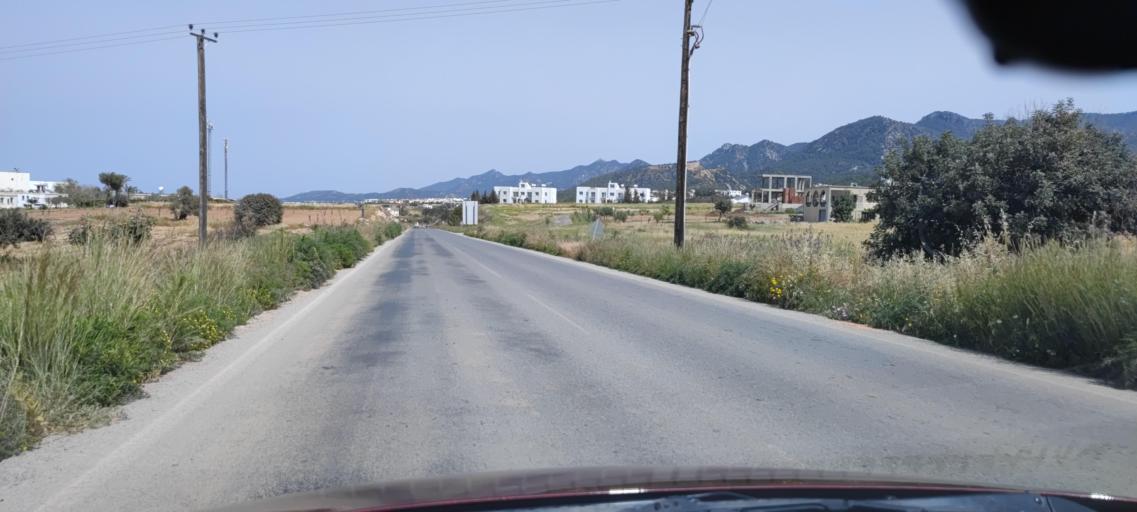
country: CY
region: Ammochostos
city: Lefkonoiko
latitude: 35.3529
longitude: 33.6286
